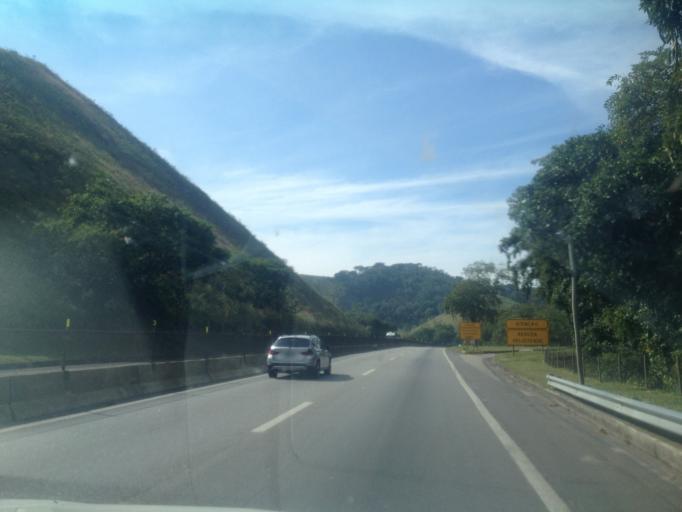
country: BR
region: Rio de Janeiro
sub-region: Pirai
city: Pirai
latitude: -22.6649
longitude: -43.8758
